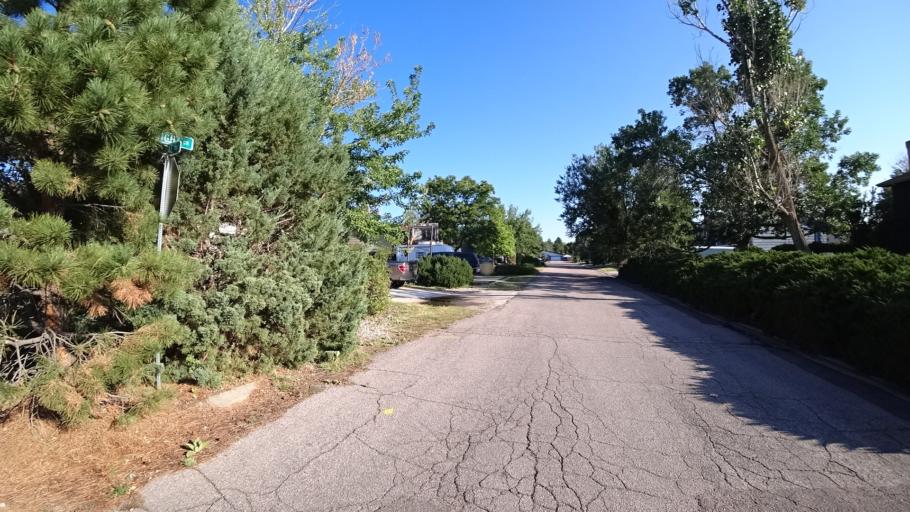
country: US
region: Colorado
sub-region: El Paso County
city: Air Force Academy
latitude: 38.9284
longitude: -104.7995
